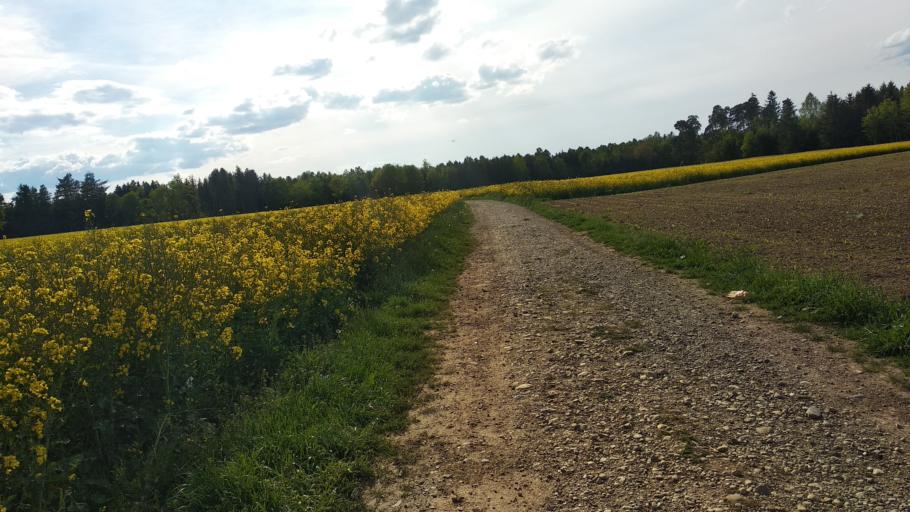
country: DE
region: Bavaria
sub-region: Upper Bavaria
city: Vaterstetten
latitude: 48.1141
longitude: 11.7655
